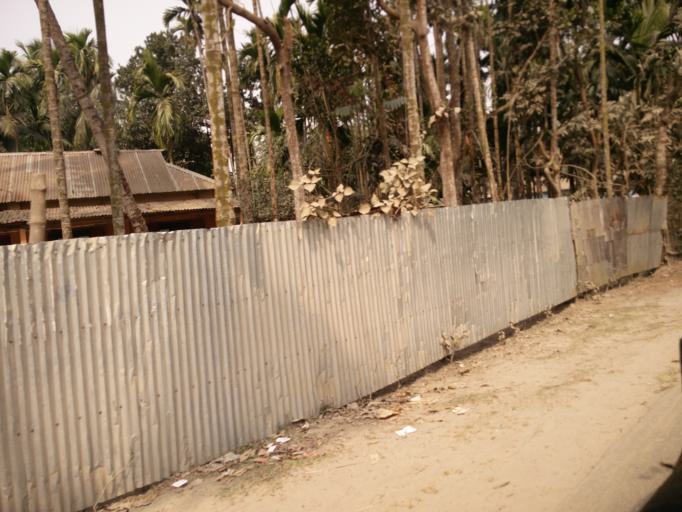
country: BD
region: Rangpur Division
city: Nageswari
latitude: 25.8876
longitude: 89.7059
